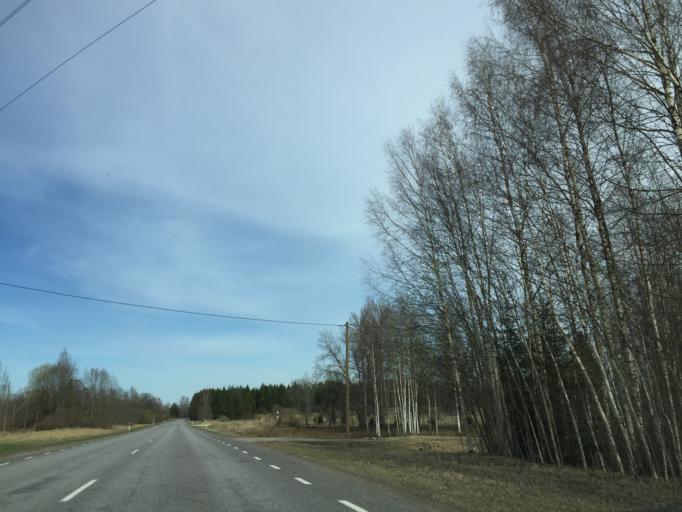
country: EE
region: Vorumaa
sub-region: Antsla vald
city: Vana-Antsla
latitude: 57.9285
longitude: 26.3424
